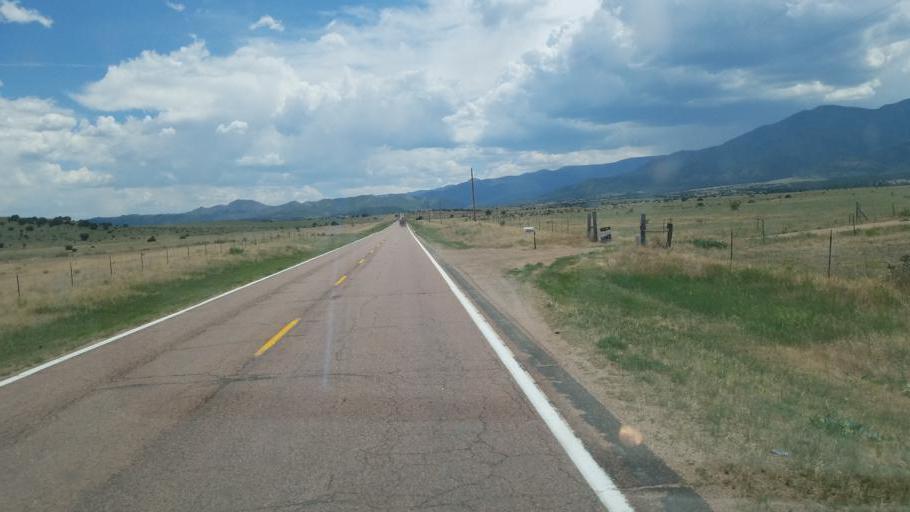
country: US
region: Colorado
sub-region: Fremont County
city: Florence
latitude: 38.2834
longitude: -105.0876
